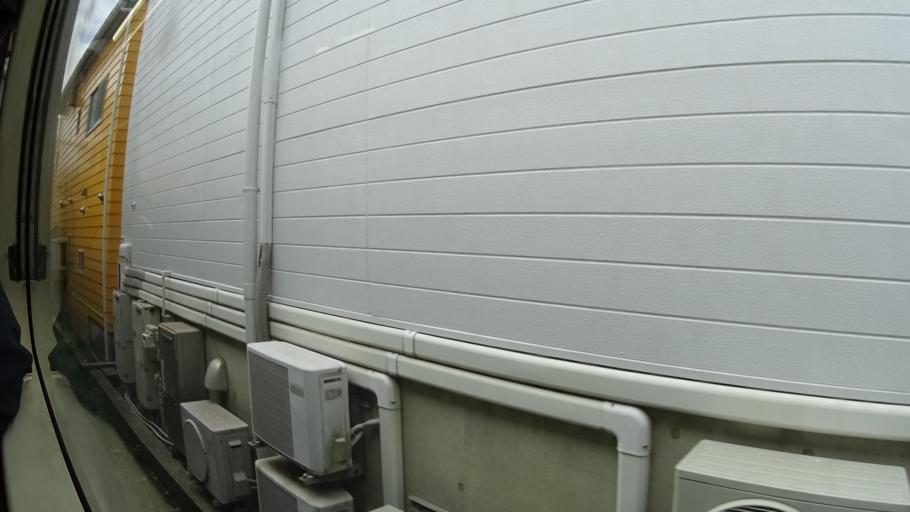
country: JP
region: Kanagawa
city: Fujisawa
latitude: 35.3124
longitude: 139.4858
